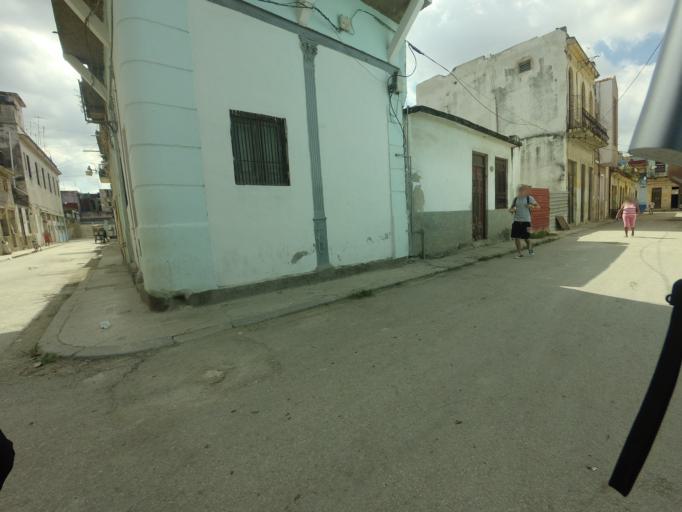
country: CU
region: La Habana
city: La Habana Vieja
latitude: 23.1308
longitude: -82.3528
